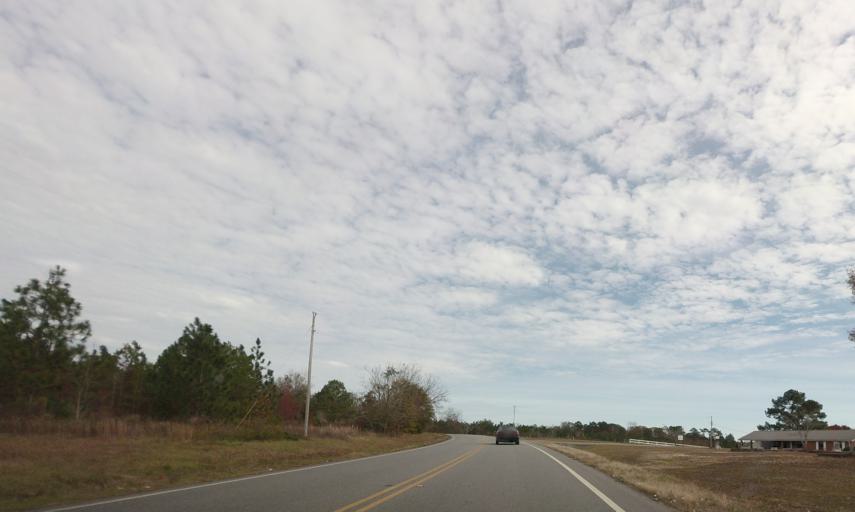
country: US
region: Georgia
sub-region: Dodge County
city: Chester
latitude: 32.4125
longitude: -83.1989
